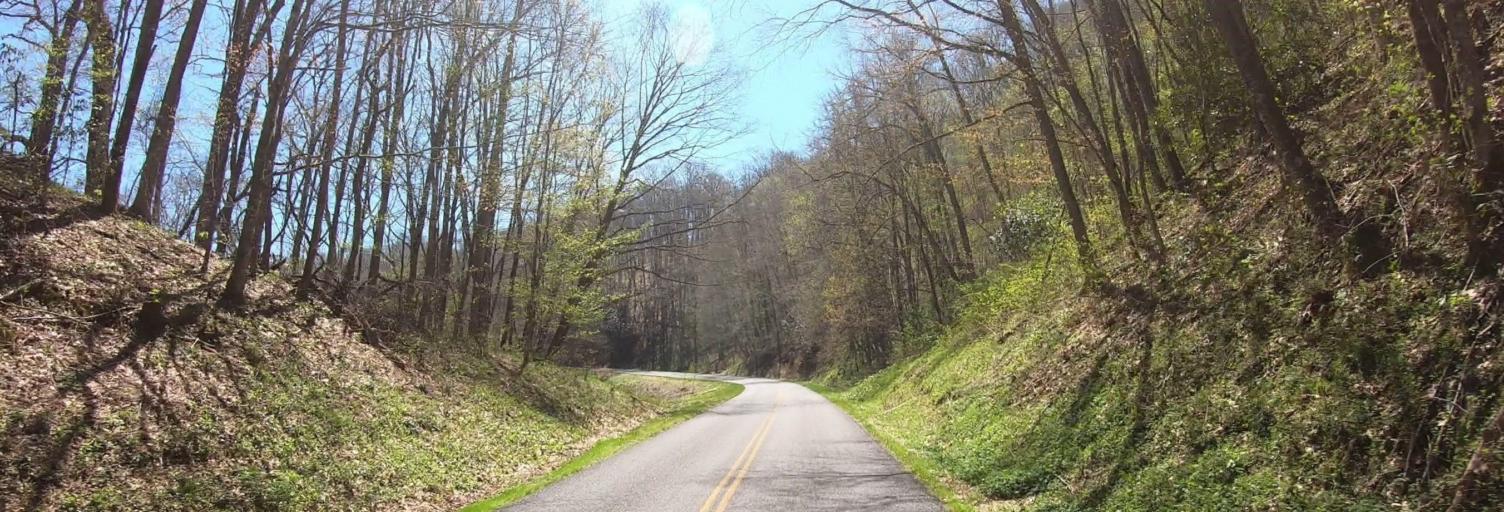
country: US
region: North Carolina
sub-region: Swain County
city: Cherokee
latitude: 35.5256
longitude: -83.2339
